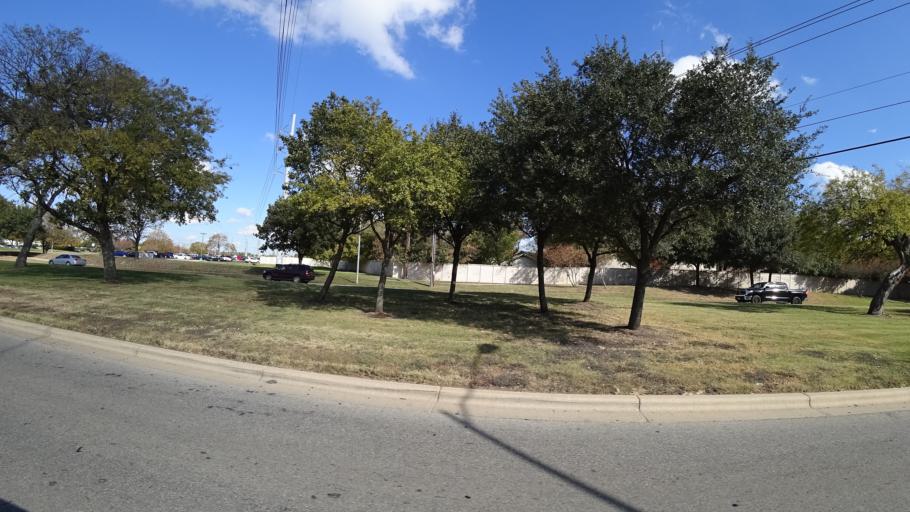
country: US
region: Texas
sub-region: Travis County
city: Wells Branch
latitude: 30.4412
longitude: -97.6878
